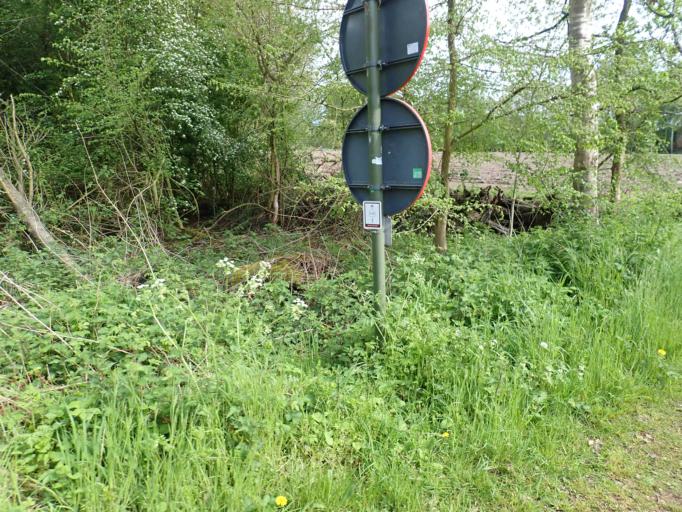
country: BE
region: Flanders
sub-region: Provincie Antwerpen
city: Puurs
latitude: 51.0679
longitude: 4.2659
